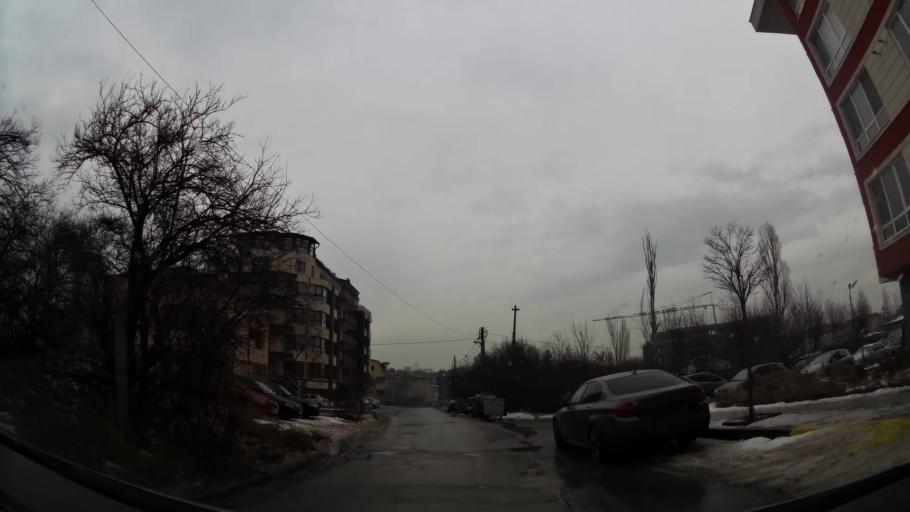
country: BG
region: Sofia-Capital
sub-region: Stolichna Obshtina
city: Sofia
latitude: 42.6558
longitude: 23.2976
